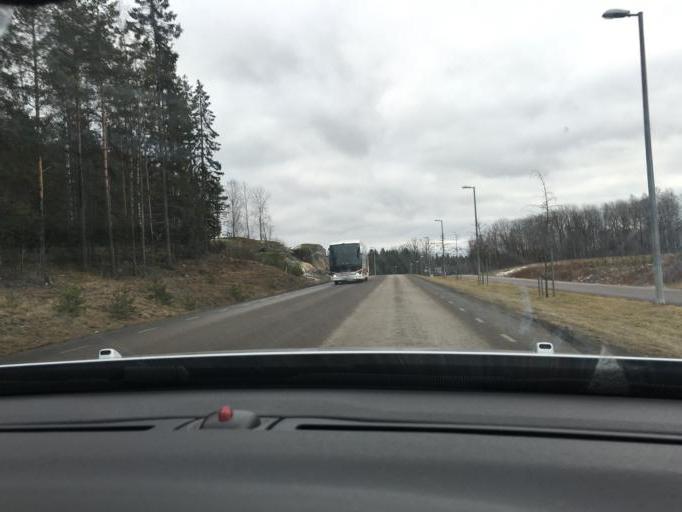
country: SE
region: Soedermanland
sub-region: Katrineholms Kommun
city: Katrineholm
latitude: 58.9963
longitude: 16.2419
